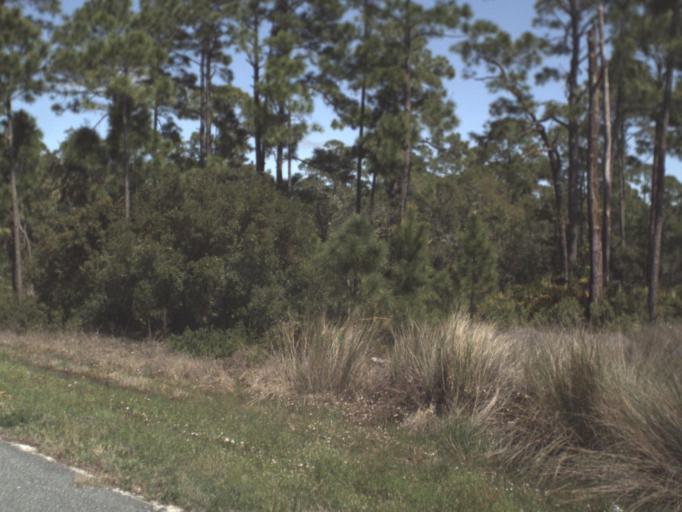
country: US
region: Florida
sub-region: Wakulla County
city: Crawfordville
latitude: 29.9826
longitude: -84.3841
